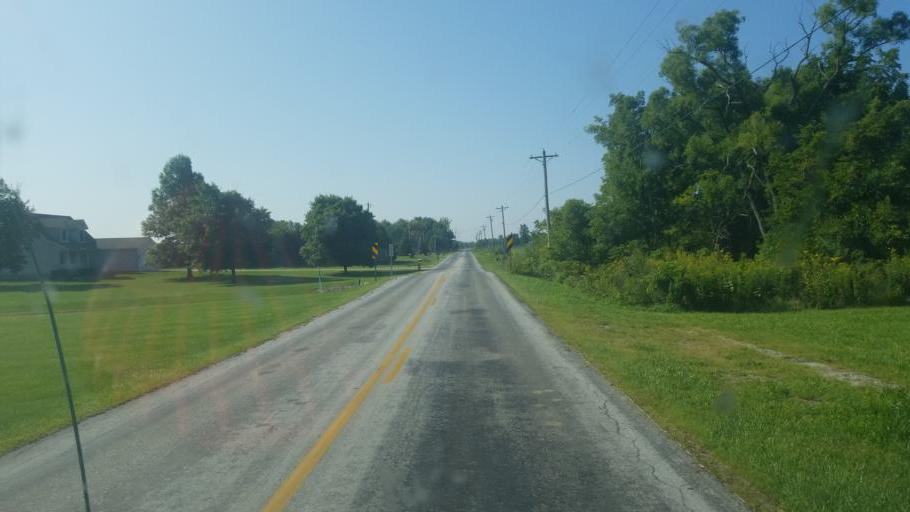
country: US
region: Ohio
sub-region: Lorain County
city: Wellington
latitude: 41.0983
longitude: -82.1613
